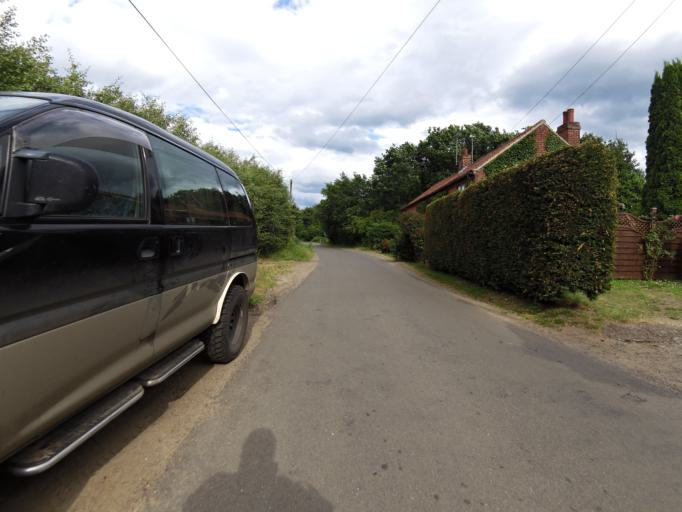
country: GB
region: England
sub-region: Suffolk
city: Beccles
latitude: 52.4696
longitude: 1.5100
